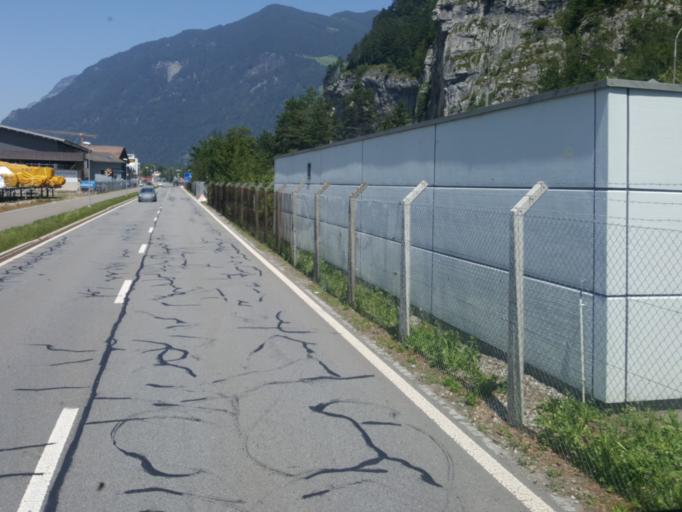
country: CH
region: Uri
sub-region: Uri
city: Schattdorf
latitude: 46.8496
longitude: 8.6459
